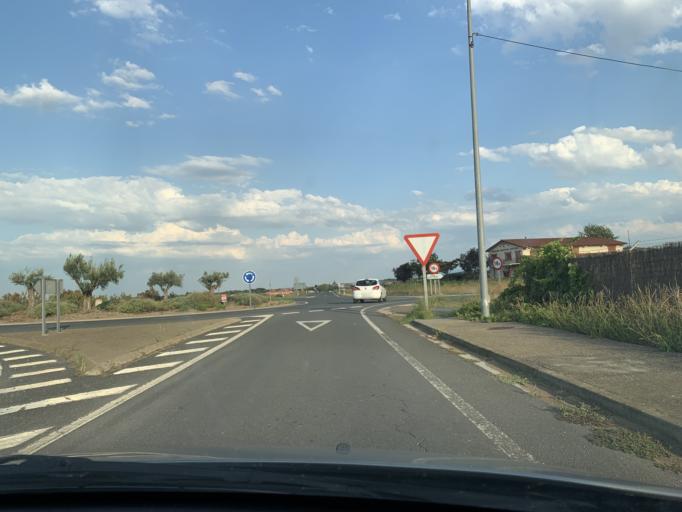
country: ES
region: La Rioja
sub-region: Provincia de La Rioja
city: Cuzcurrita de Rio Tiron
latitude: 42.5518
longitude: -2.9635
